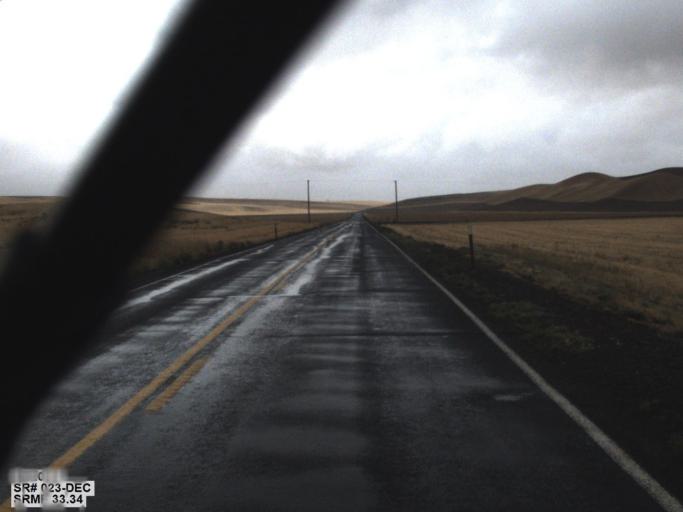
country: US
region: Washington
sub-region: Spokane County
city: Cheney
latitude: 47.1865
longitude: -117.8713
